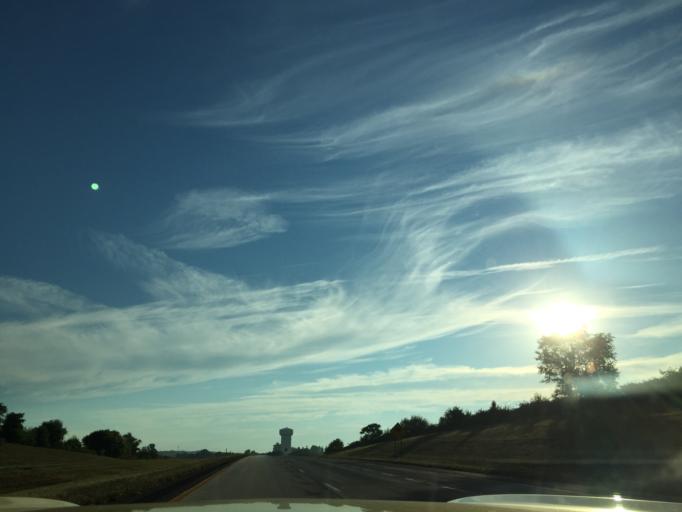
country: US
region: Pennsylvania
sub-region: Berks County
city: Kutztown
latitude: 40.5074
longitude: -75.8017
